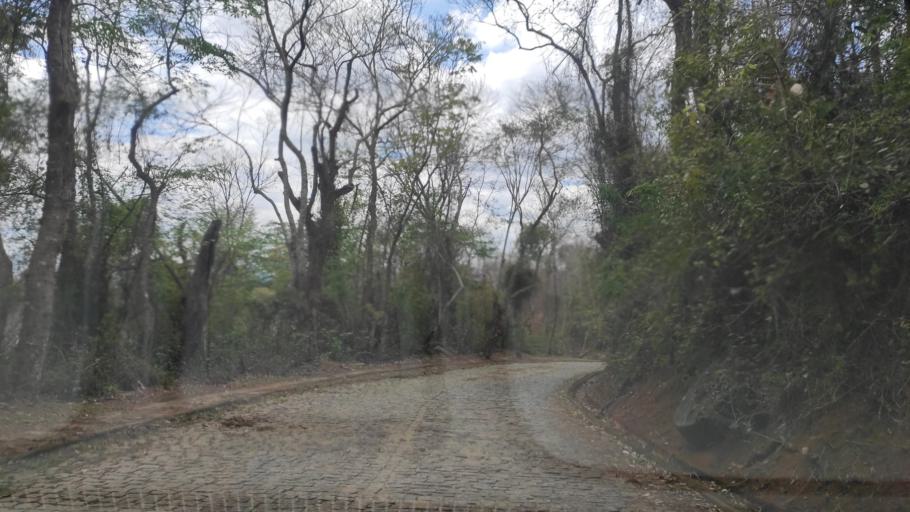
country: BR
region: Espirito Santo
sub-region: Vitoria
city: Vitoria
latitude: -20.3030
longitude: -40.3394
